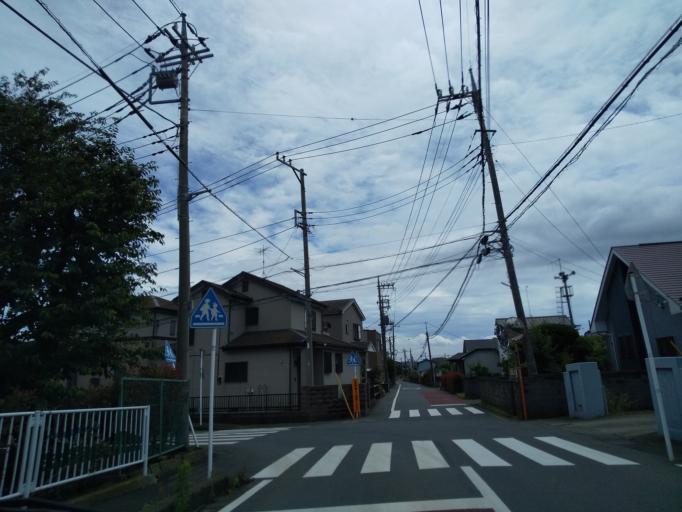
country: JP
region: Kanagawa
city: Zama
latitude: 35.4961
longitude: 139.3380
